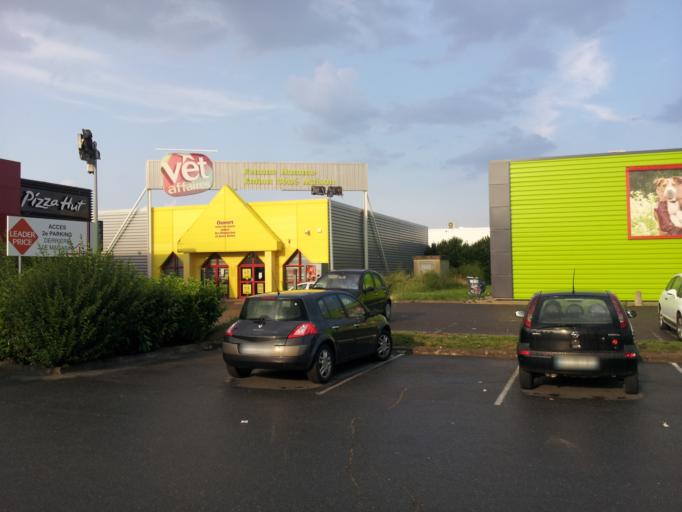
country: FR
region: Ile-de-France
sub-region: Departement de l'Essonne
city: Fleury-Merogis
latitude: 48.6255
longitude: 2.3459
